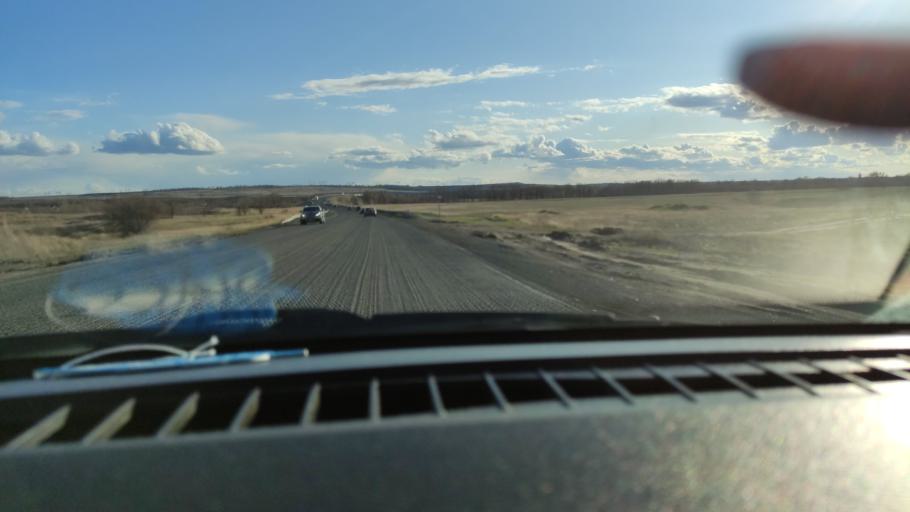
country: RU
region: Saratov
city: Yelshanka
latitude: 51.8048
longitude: 46.1932
